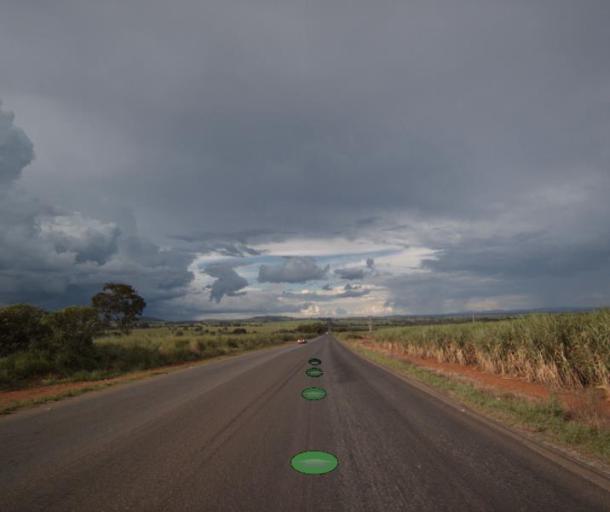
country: BR
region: Goias
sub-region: Ceres
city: Ceres
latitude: -15.1433
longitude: -49.5294
